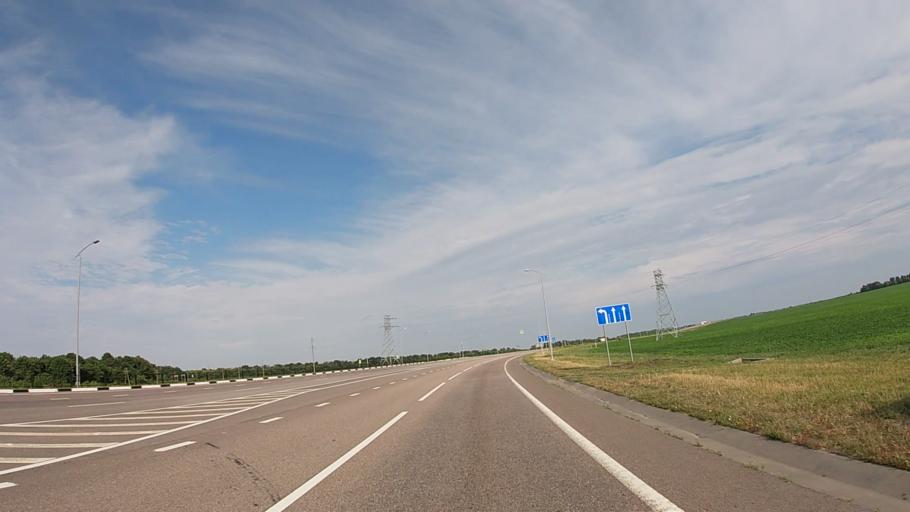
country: RU
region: Belgorod
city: Rakitnoye
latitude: 50.7906
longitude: 35.8688
